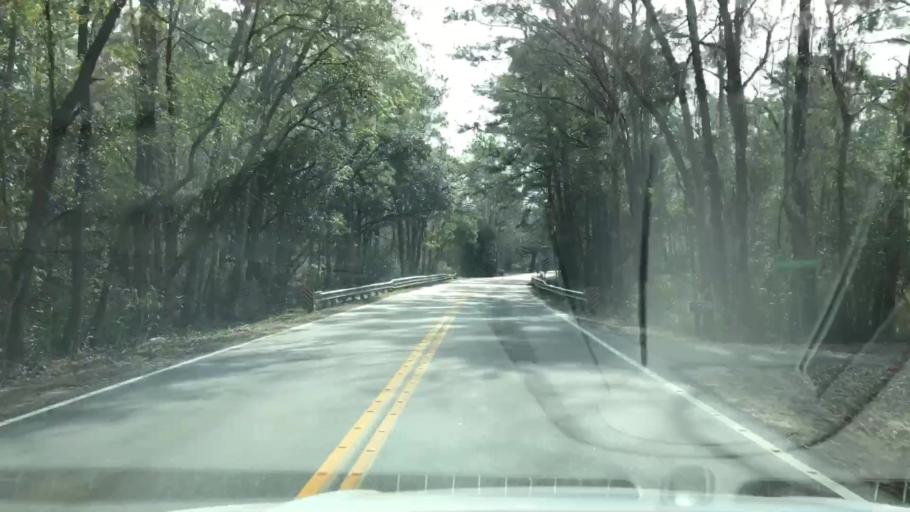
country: US
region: South Carolina
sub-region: Charleston County
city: Folly Beach
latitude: 32.7160
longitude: -80.0201
